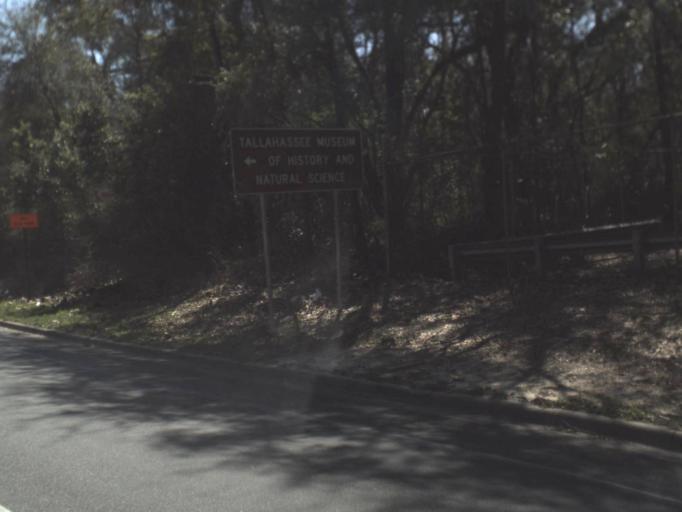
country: US
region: Florida
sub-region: Leon County
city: Tallahassee
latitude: 30.4199
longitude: -84.3506
